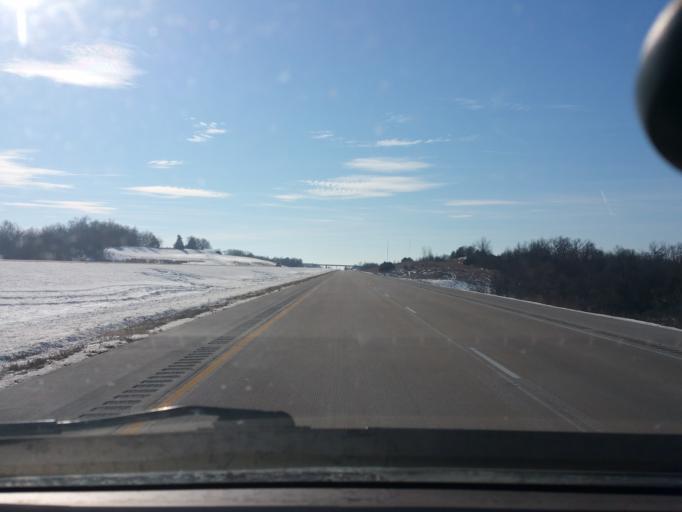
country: US
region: Iowa
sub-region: Clarke County
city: Osceola
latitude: 40.8844
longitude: -93.8012
